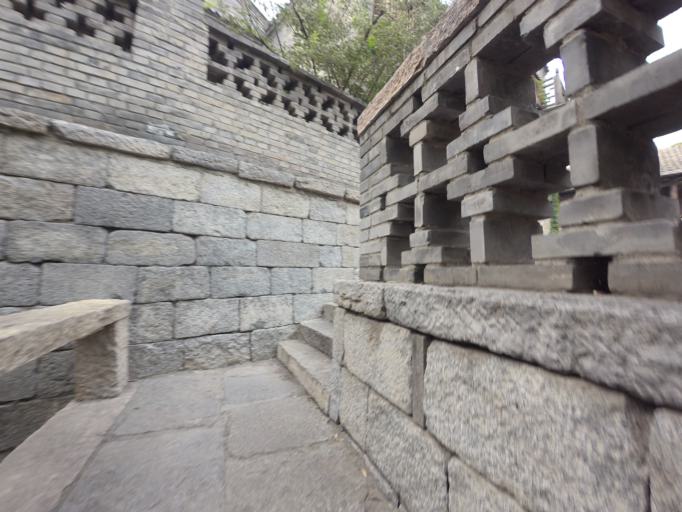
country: CN
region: Beijing
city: Xinchengzi
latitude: 40.6517
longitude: 117.2716
